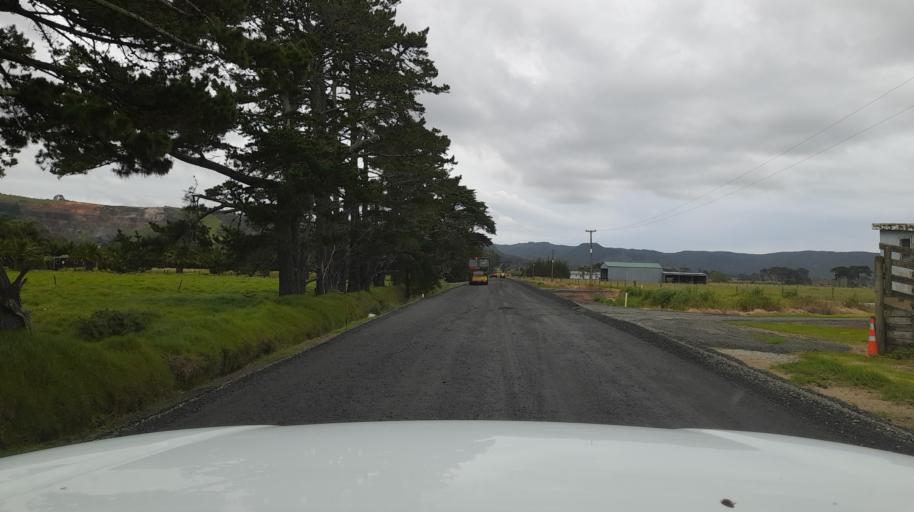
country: NZ
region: Northland
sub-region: Far North District
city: Ahipara
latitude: -35.1563
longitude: 173.1895
